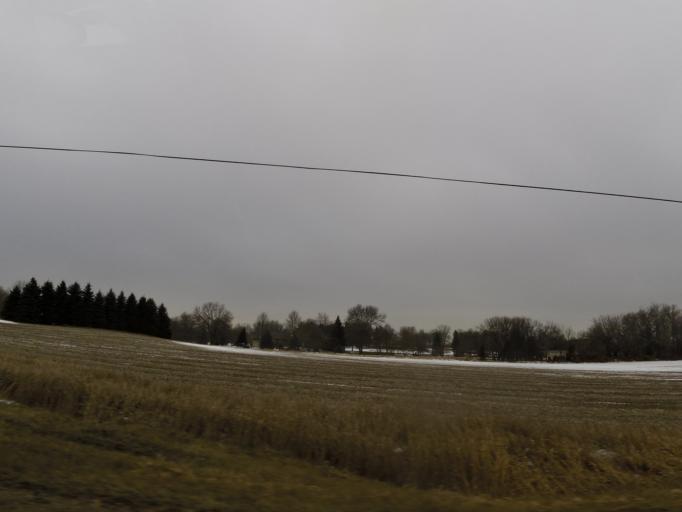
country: US
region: Minnesota
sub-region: Carver County
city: Carver
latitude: 44.7764
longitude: -93.7013
